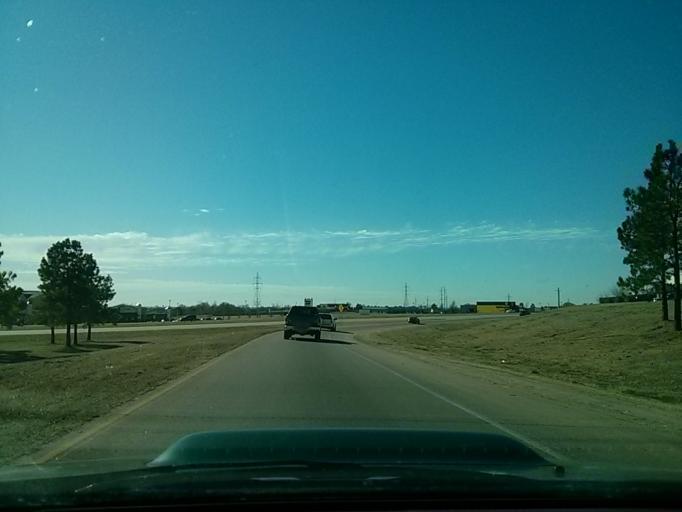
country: US
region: Oklahoma
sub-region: Tulsa County
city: Owasso
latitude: 36.2924
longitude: -95.8373
